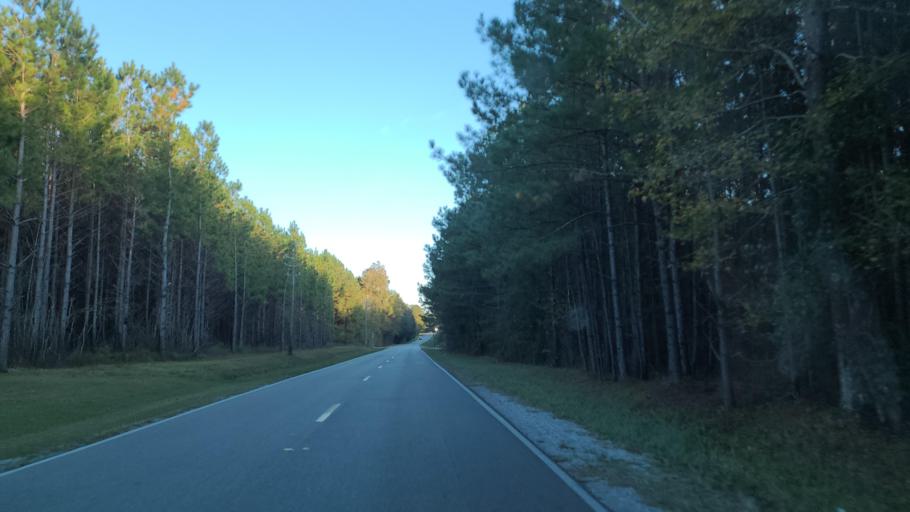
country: US
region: Mississippi
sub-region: Lamar County
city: Lumberton
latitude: 30.9997
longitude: -89.4101
